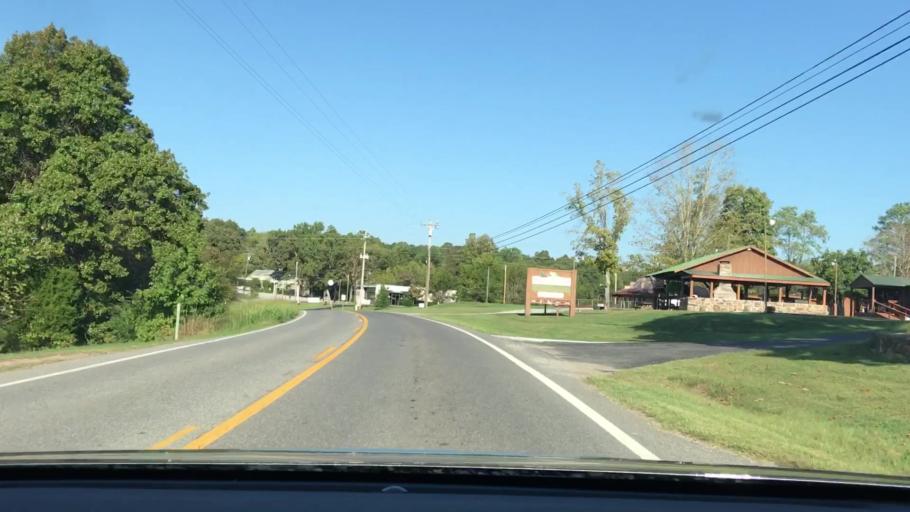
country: US
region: Kentucky
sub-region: Marshall County
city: Benton
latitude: 36.7764
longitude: -88.1442
